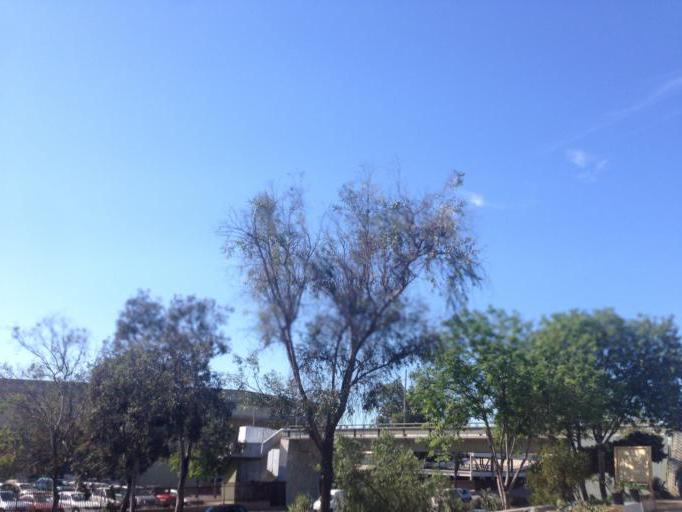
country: MX
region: Baja California
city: Tijuana
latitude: 32.5286
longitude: -117.0179
